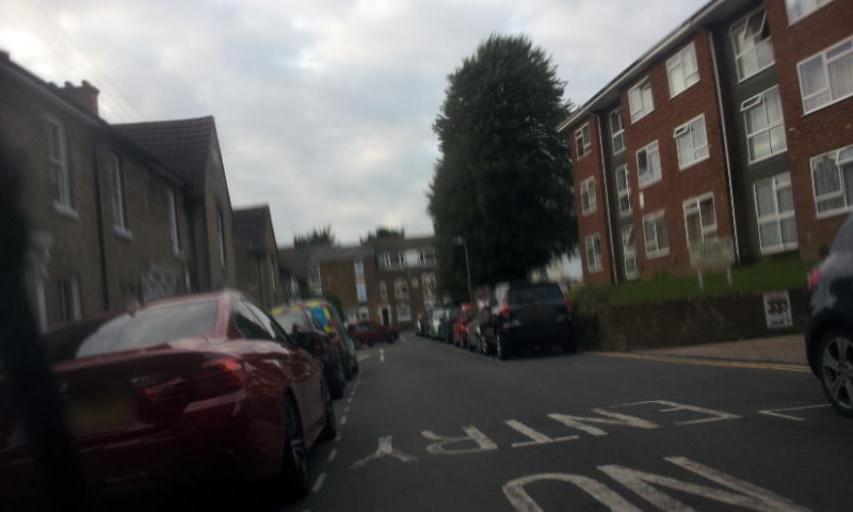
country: GB
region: England
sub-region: Kent
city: Maidstone
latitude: 51.2806
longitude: 0.5224
